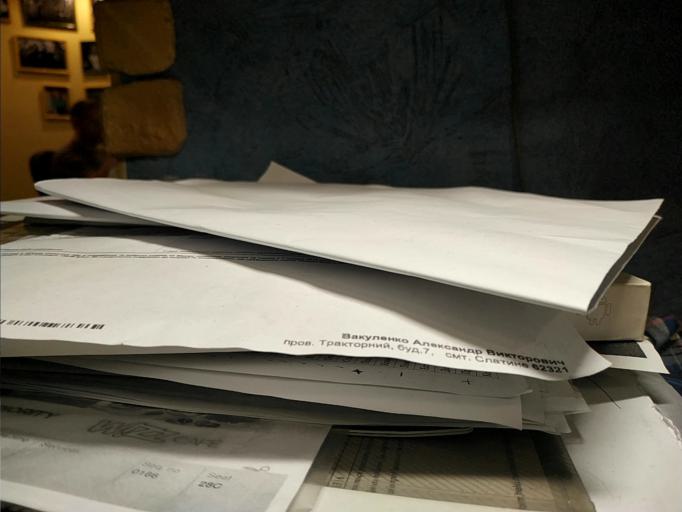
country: RU
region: Tverskaya
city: Zubtsov
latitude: 56.1188
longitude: 34.5812
